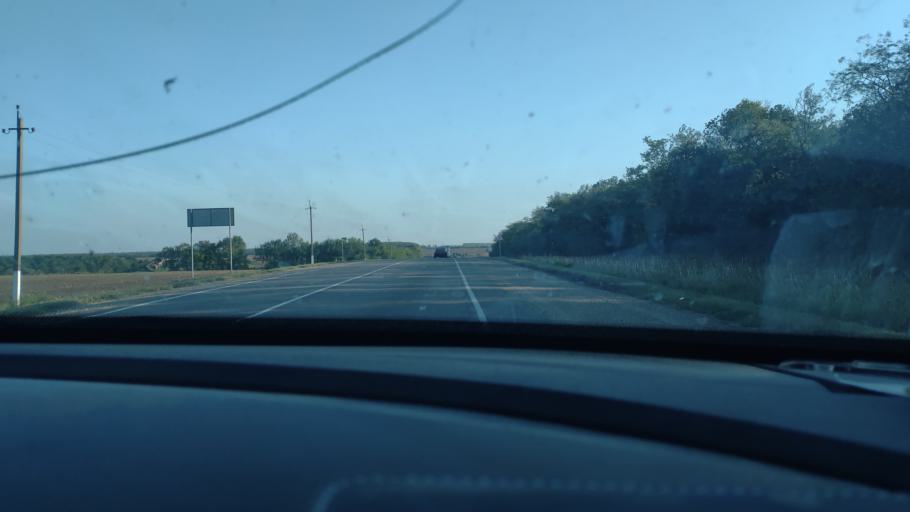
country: RU
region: Krasnodarskiy
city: Novominskaya
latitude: 46.2972
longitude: 38.9333
